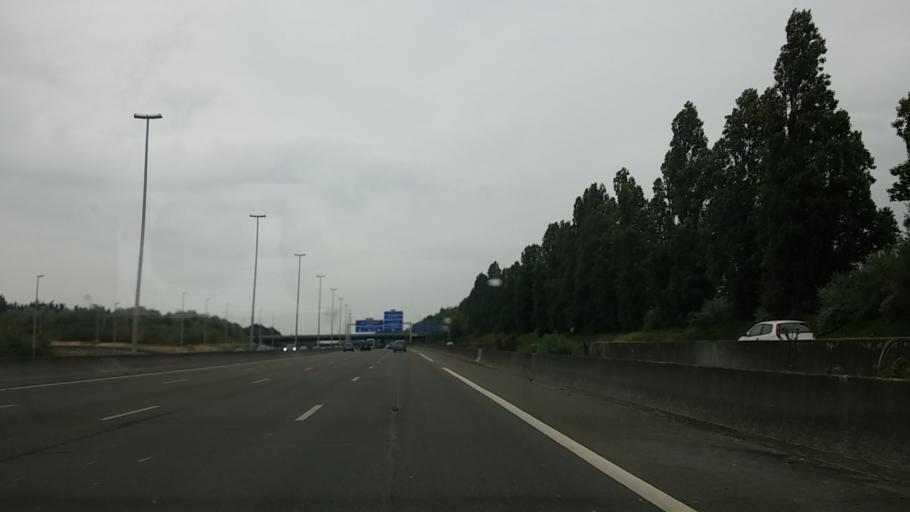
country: FR
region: Ile-de-France
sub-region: Departement de Seine-Saint-Denis
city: Le Blanc-Mesnil
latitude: 48.9589
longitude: 2.4652
